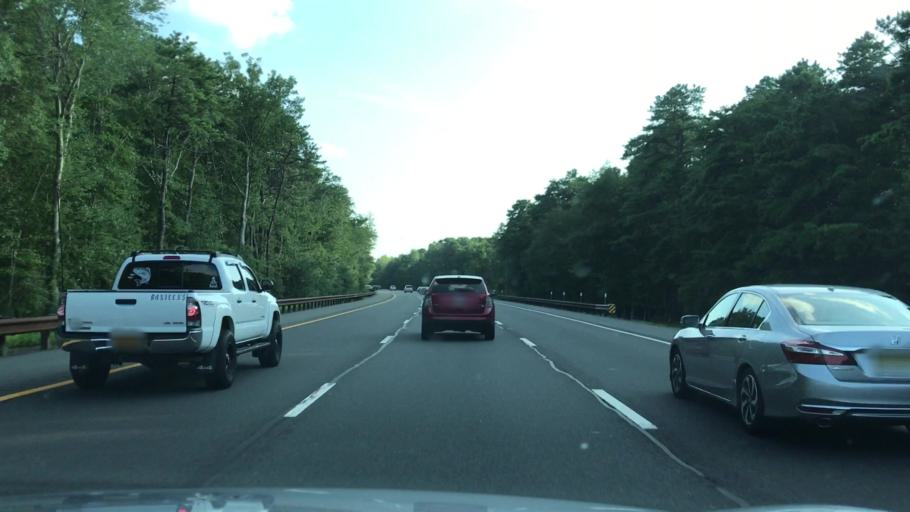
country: US
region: New Jersey
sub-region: Ocean County
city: Mystic Island
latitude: 39.6037
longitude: -74.4364
